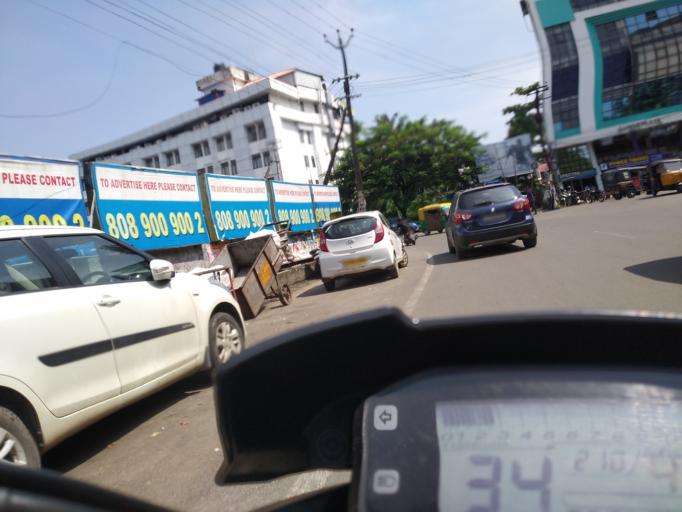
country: IN
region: Kerala
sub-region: Ernakulam
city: Cochin
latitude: 9.9784
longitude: 76.2875
